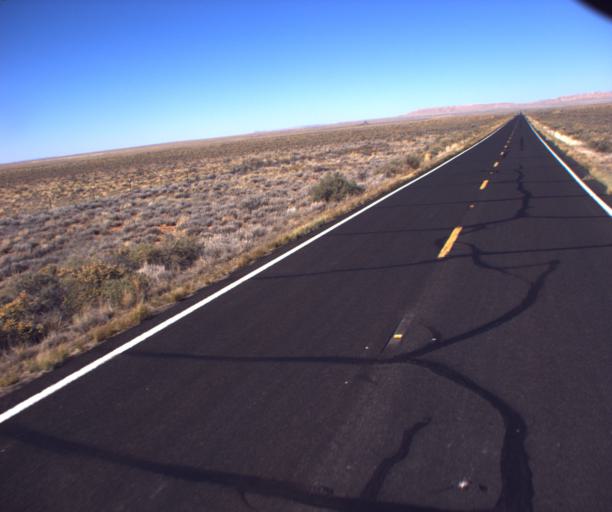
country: US
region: Arizona
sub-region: Navajo County
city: First Mesa
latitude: 35.6763
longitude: -110.4987
